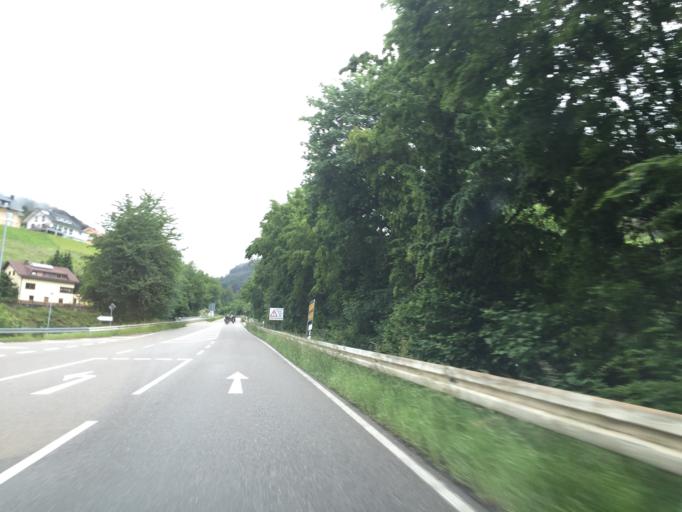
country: DE
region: Baden-Wuerttemberg
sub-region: Freiburg Region
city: Todtnau
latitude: 47.8277
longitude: 7.9418
